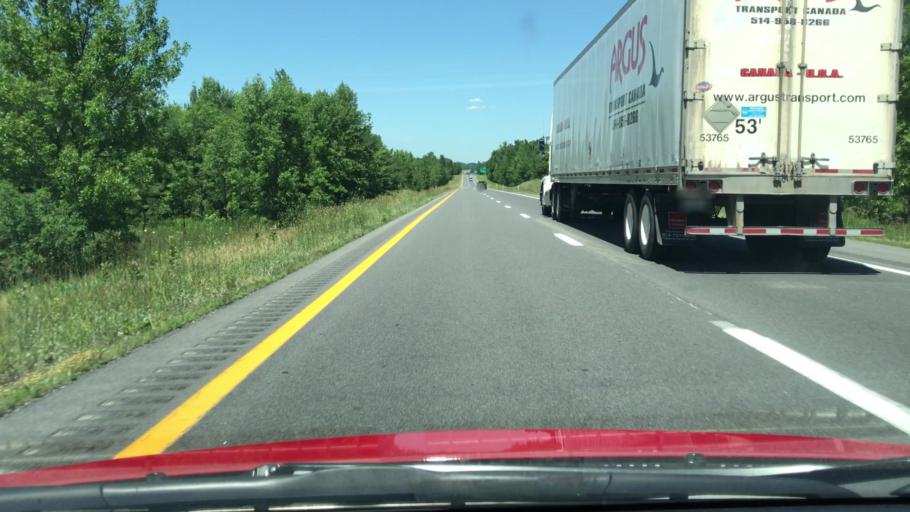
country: US
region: New York
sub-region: Clinton County
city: Cumberland Head
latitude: 44.7558
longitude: -73.4287
